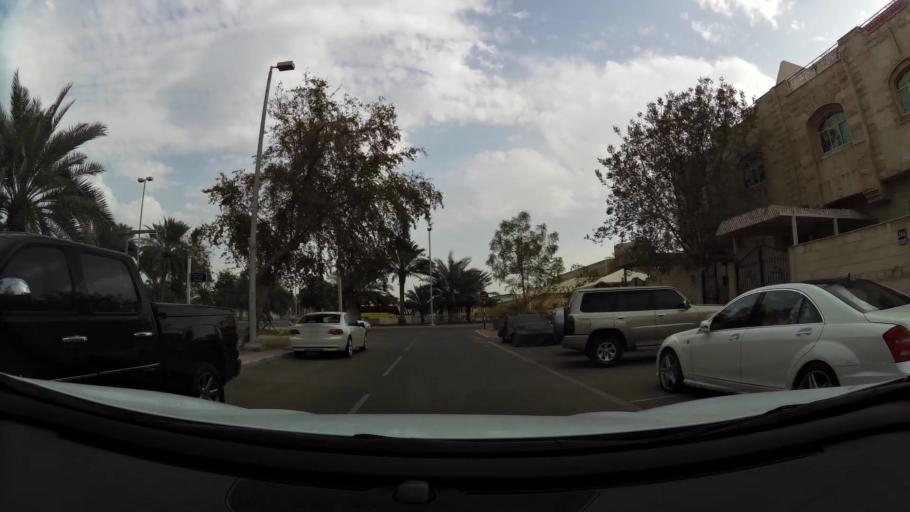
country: AE
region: Abu Dhabi
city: Abu Dhabi
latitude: 24.4610
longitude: 54.3561
